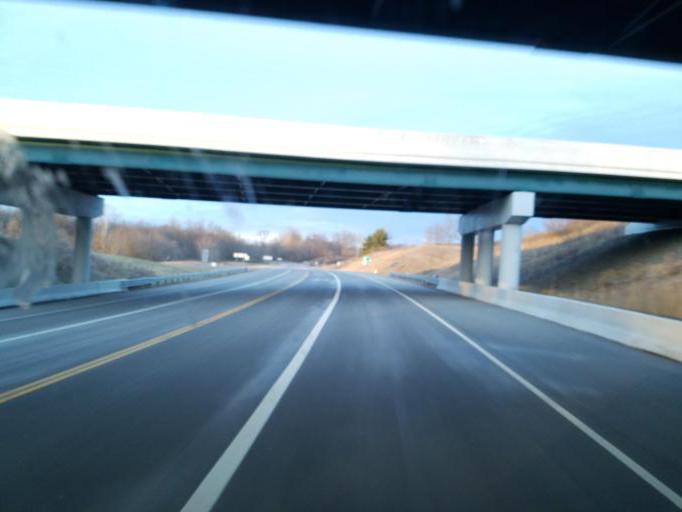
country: US
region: Ohio
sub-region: Muskingum County
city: Dresden
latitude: 40.1549
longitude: -82.0259
